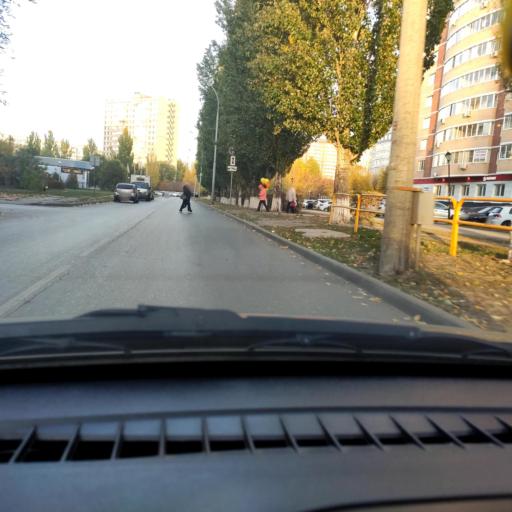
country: RU
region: Samara
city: Tol'yatti
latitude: 53.5403
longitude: 49.3234
